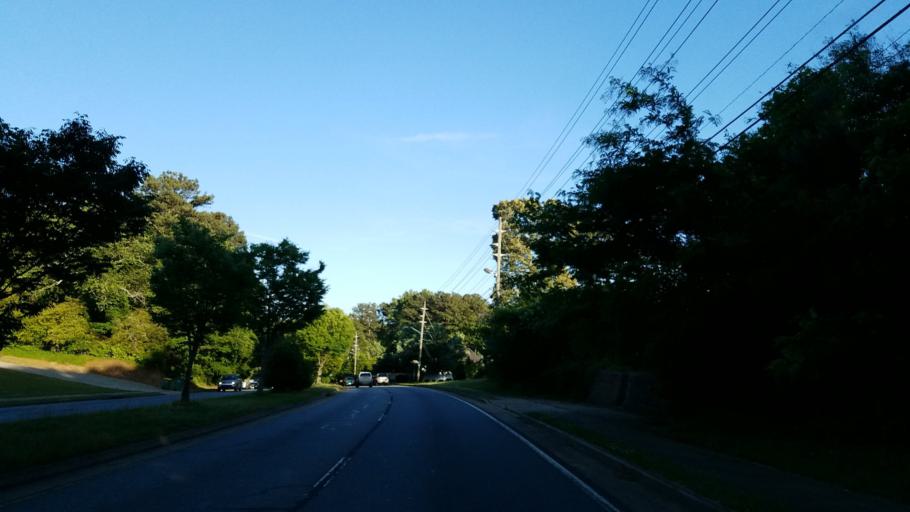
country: US
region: Georgia
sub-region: Cherokee County
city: Woodstock
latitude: 34.0670
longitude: -84.5658
